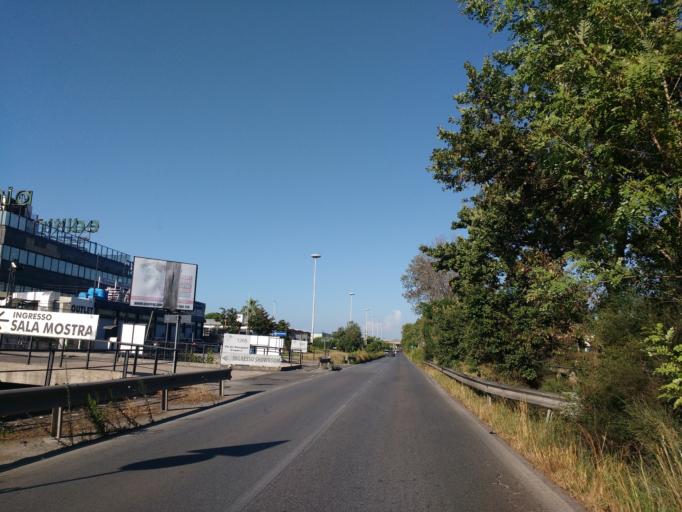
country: IT
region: Latium
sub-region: Citta metropolitana di Roma Capitale
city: Acilia-Castel Fusano-Ostia Antica
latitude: 41.7726
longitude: 12.3316
